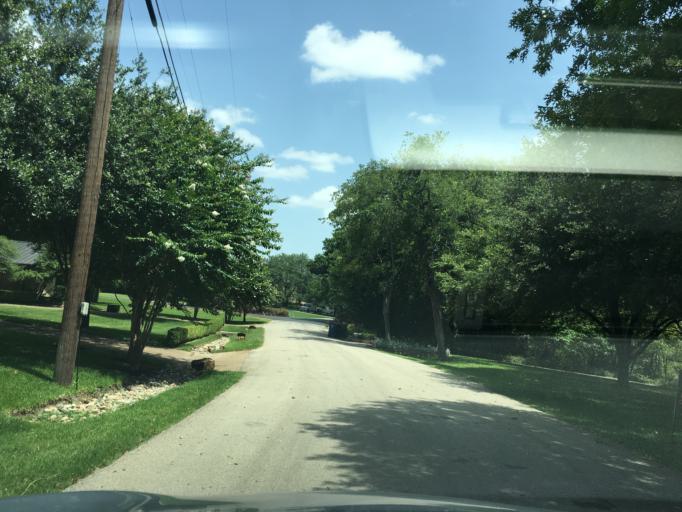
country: US
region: Texas
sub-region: Dallas County
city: University Park
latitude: 32.9028
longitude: -96.7906
